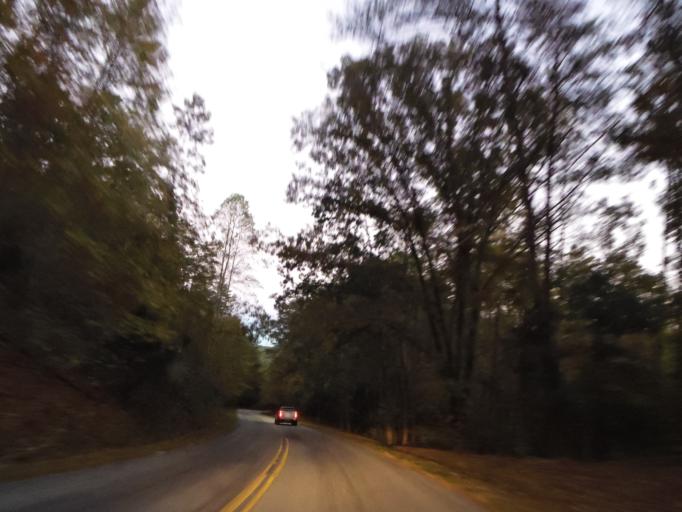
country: US
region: Tennessee
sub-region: Blount County
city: Wildwood
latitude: 35.7178
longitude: -83.8296
